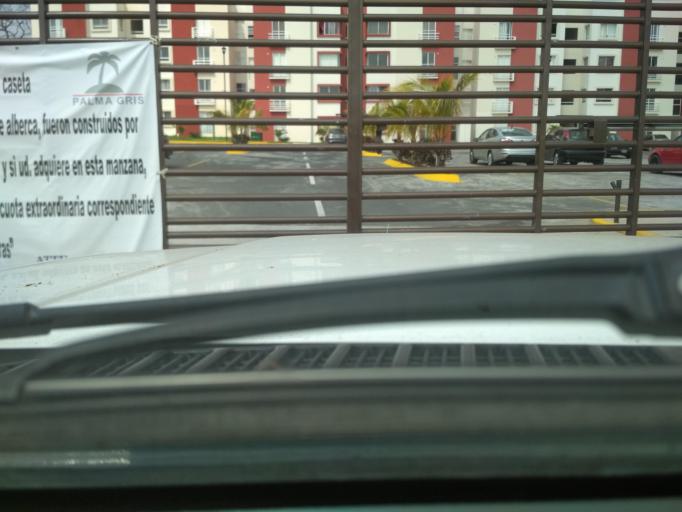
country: MX
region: Veracruz
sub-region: Veracruz
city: Lomas de Rio Medio Cuatro
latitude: 19.1795
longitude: -96.2100
